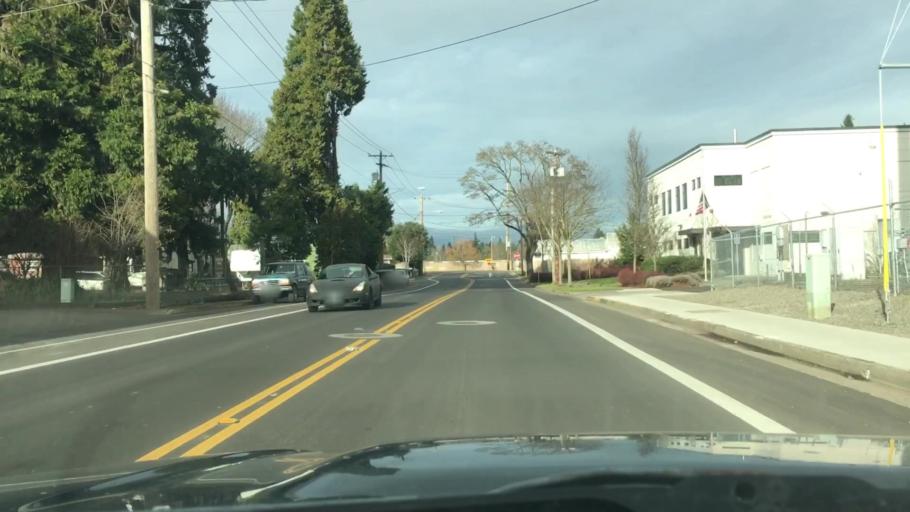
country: US
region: Oregon
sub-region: Lane County
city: Eugene
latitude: 44.0618
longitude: -123.1226
